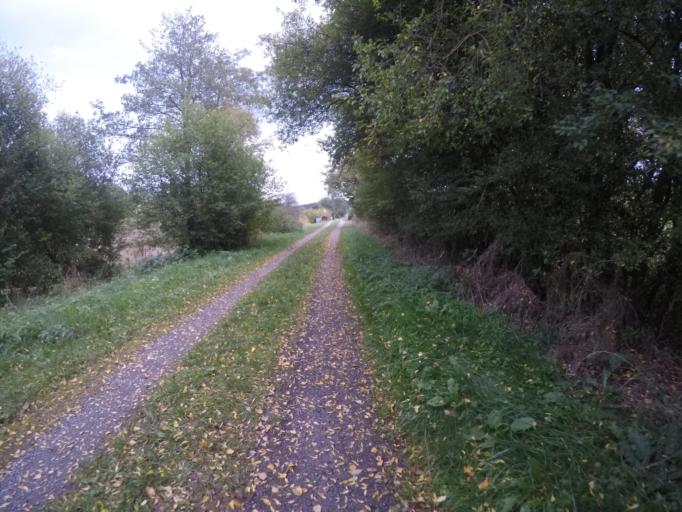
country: BE
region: Wallonia
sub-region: Province du Luxembourg
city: Fauvillers
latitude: 49.8813
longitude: 5.6737
